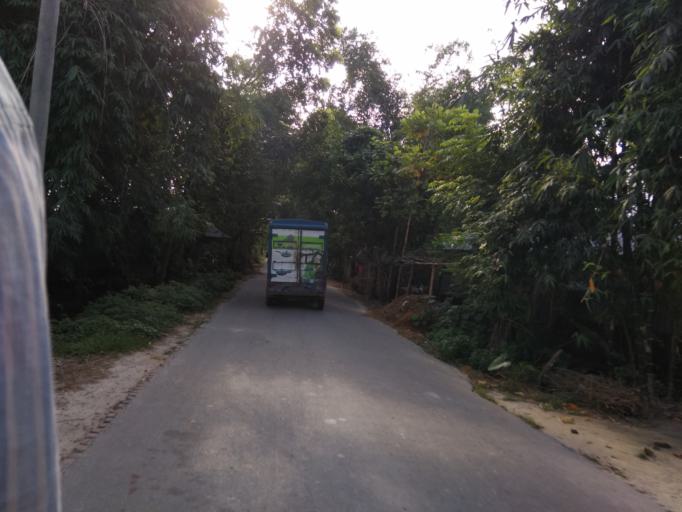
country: BD
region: Rangpur Division
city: Rangpur
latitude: 25.8308
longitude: 89.1175
